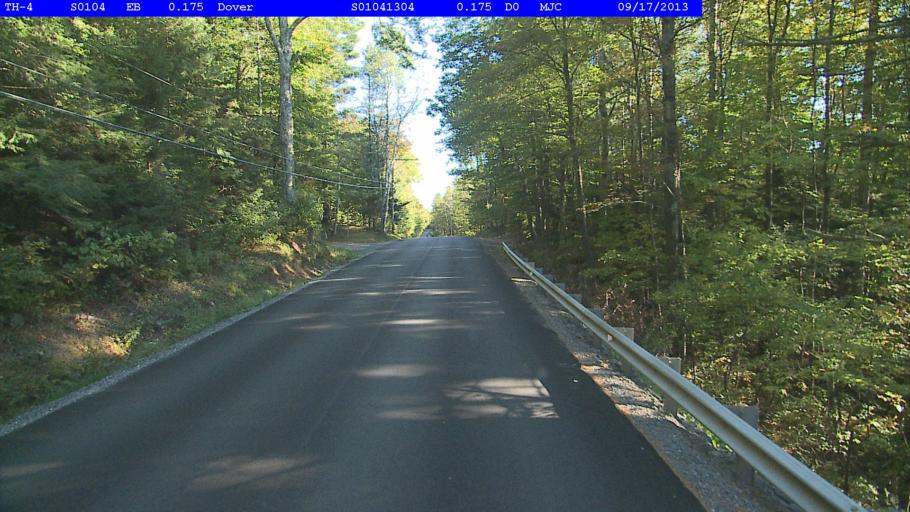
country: US
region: Vermont
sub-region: Windham County
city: Dover
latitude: 42.9347
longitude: -72.8476
